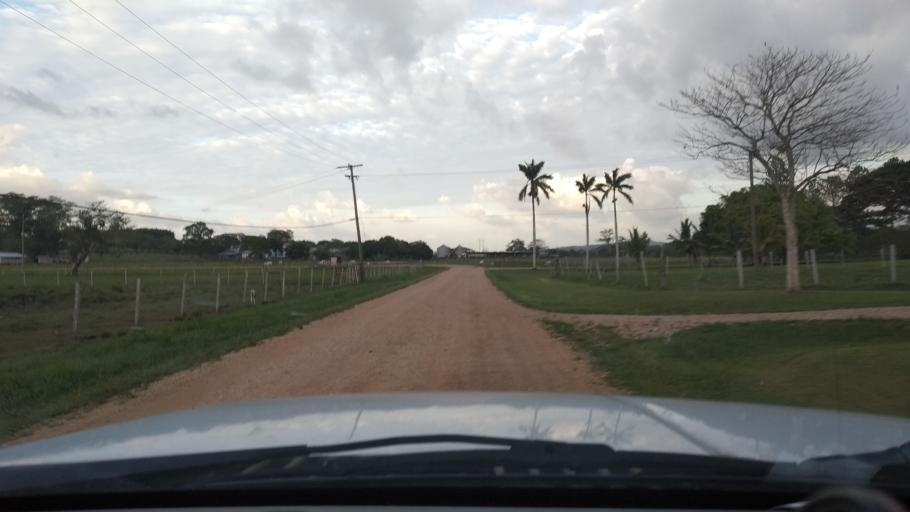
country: BZ
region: Cayo
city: San Ignacio
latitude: 17.2242
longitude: -88.9942
